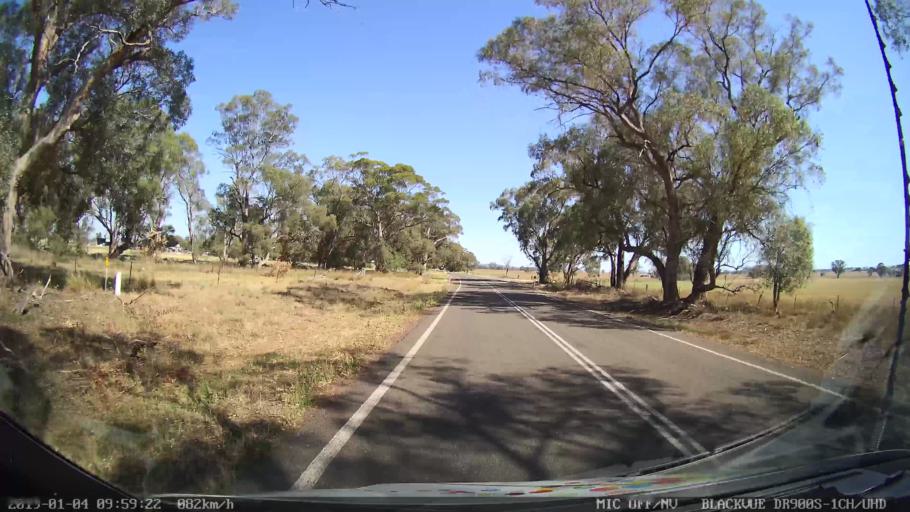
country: AU
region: New South Wales
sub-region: Cabonne
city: Canowindra
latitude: -33.5083
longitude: 148.3867
